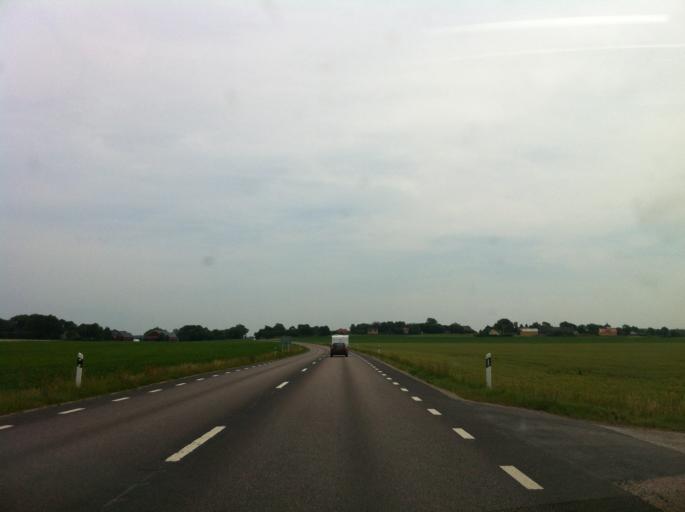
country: SE
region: Blekinge
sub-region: Karlskrona Kommun
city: Jaemjoe
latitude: 56.1834
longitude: 15.7424
